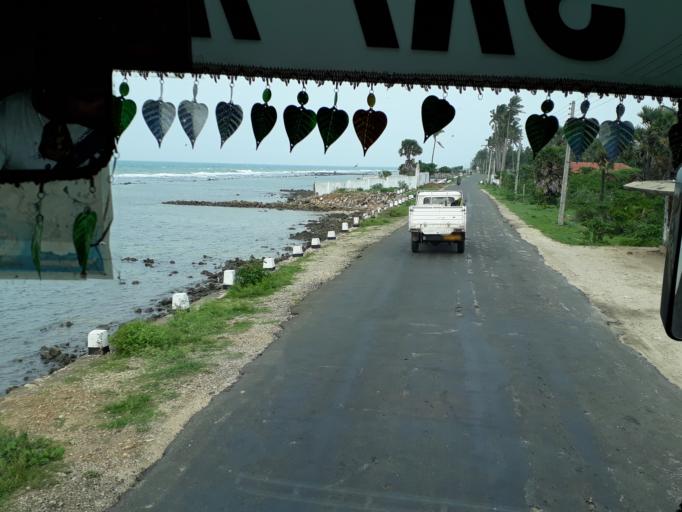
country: LK
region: Northern Province
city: Point Pedro
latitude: 9.8320
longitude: 80.2016
